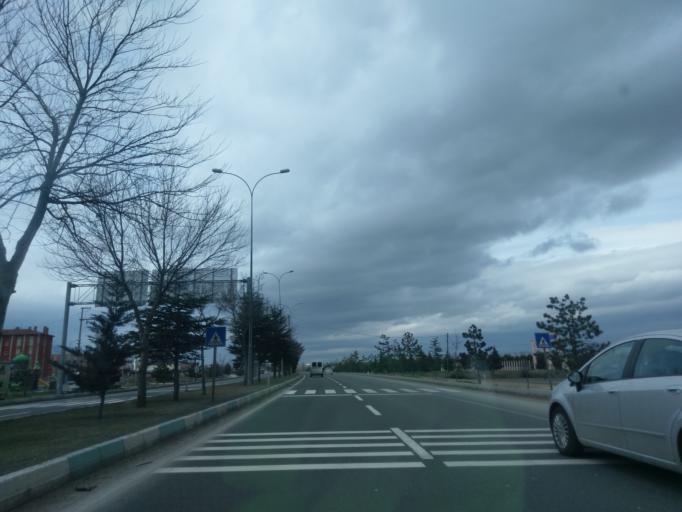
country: TR
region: Kuetahya
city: Kutahya
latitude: 39.4092
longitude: 30.0233
